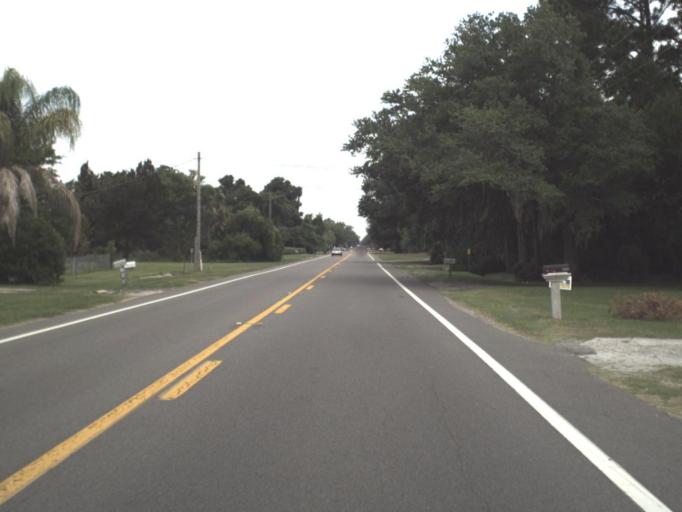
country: US
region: Florida
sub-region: Duval County
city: Atlantic Beach
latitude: 30.4099
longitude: -81.5152
